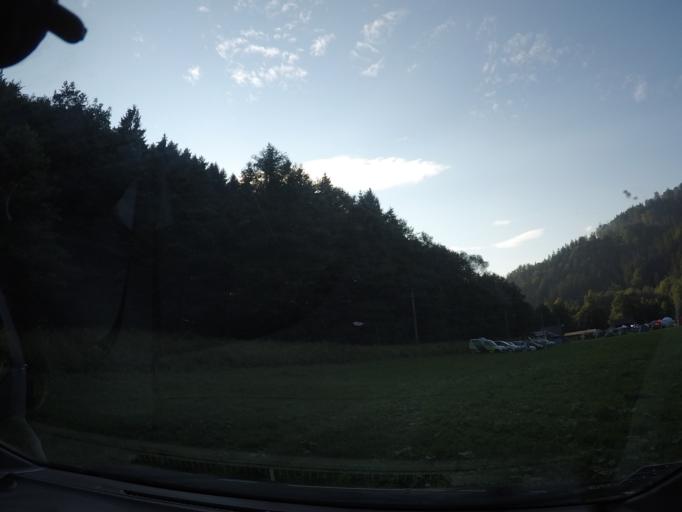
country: SK
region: Nitriansky
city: Bojnice
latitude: 48.9078
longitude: 18.6030
